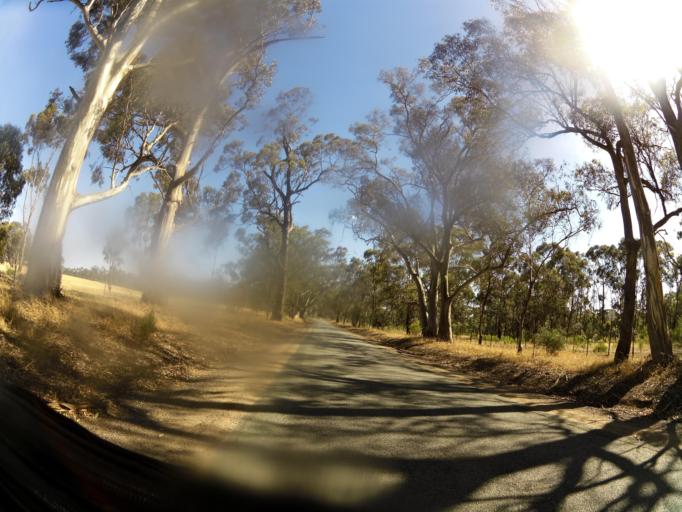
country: AU
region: Victoria
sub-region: Campaspe
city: Kyabram
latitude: -36.8749
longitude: 145.0857
